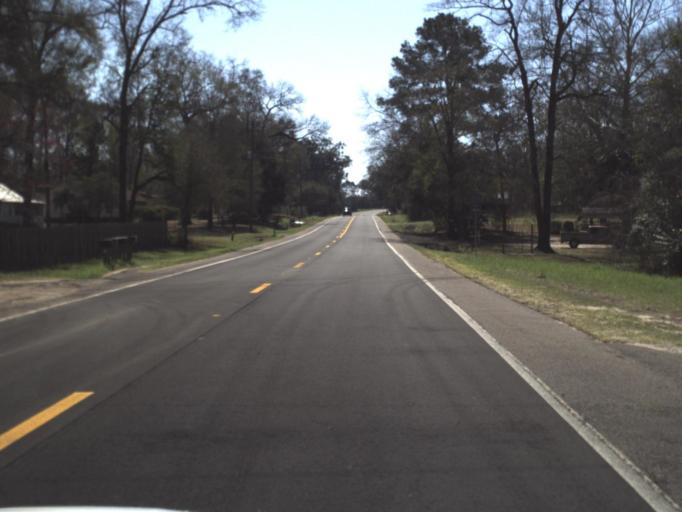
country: US
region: Florida
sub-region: Jackson County
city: Marianna
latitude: 30.6246
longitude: -85.1528
